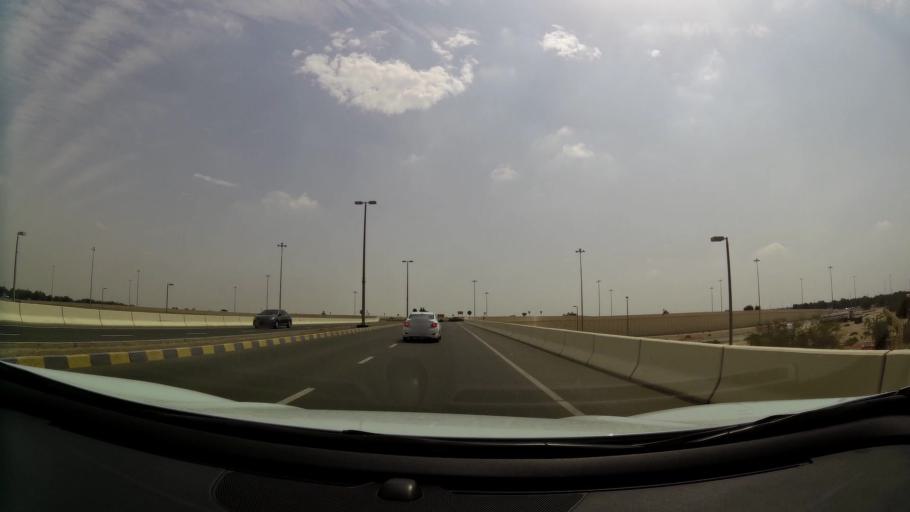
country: AE
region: Abu Dhabi
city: Abu Dhabi
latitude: 24.5127
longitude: 54.6619
